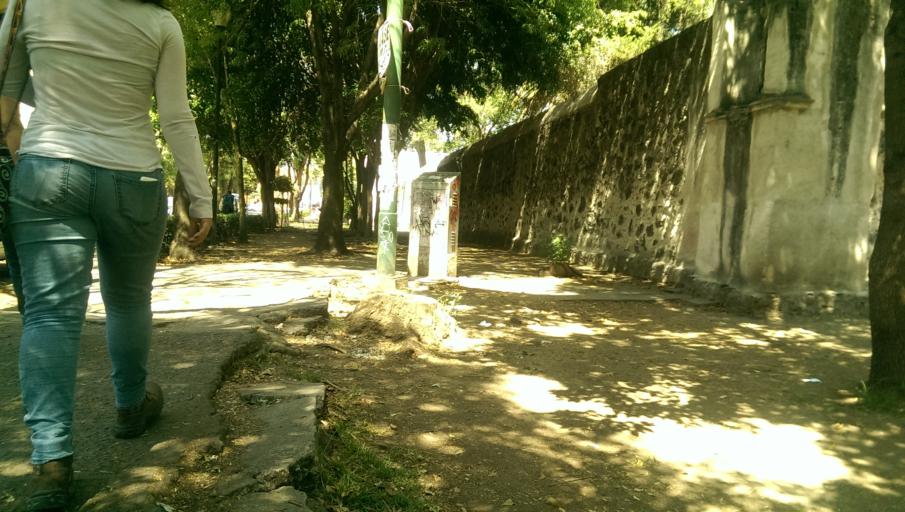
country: MX
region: Mexico City
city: Coyoacan
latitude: 19.3543
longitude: -99.1479
